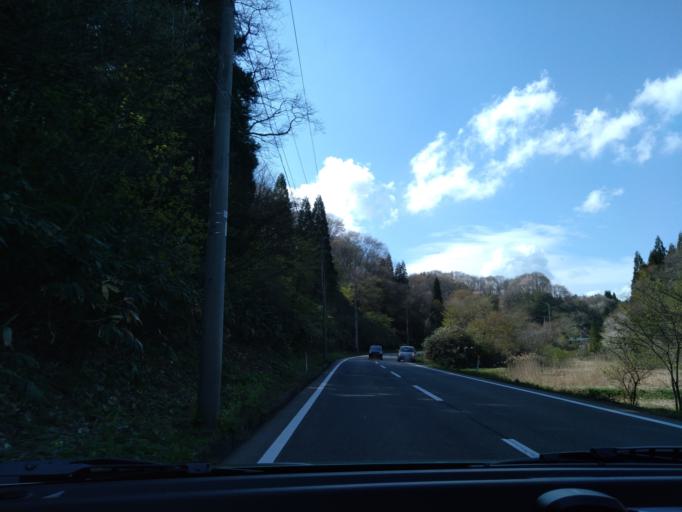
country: JP
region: Akita
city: Akita
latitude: 39.6922
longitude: 140.2238
